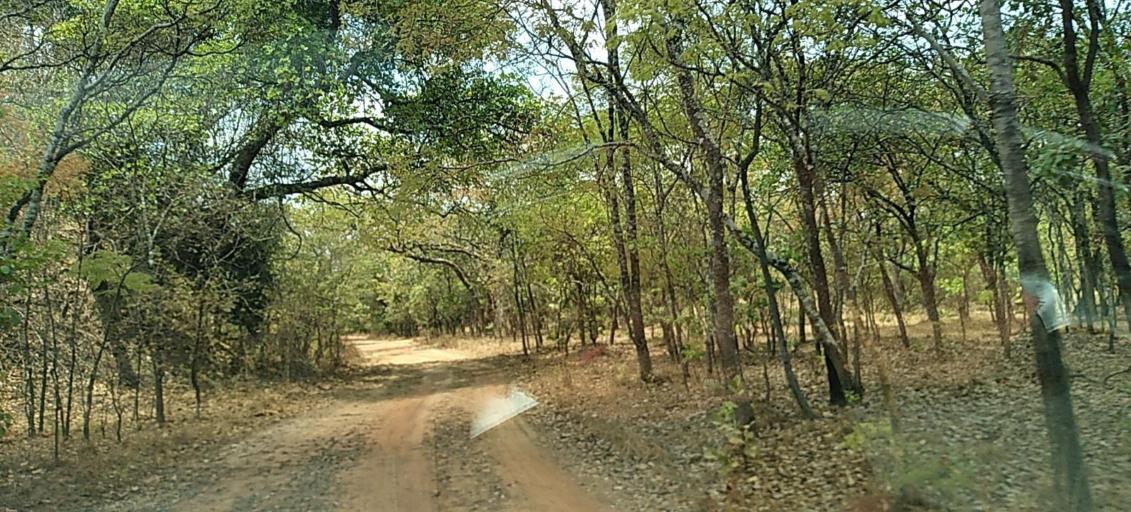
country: ZM
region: Copperbelt
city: Chililabombwe
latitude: -12.5054
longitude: 27.6353
